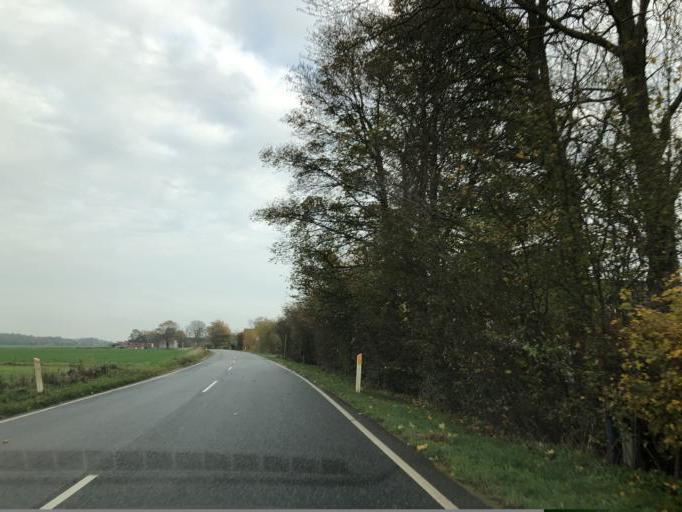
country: DK
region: Central Jutland
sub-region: Hedensted Kommune
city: Hedensted
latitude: 55.7349
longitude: 9.7675
